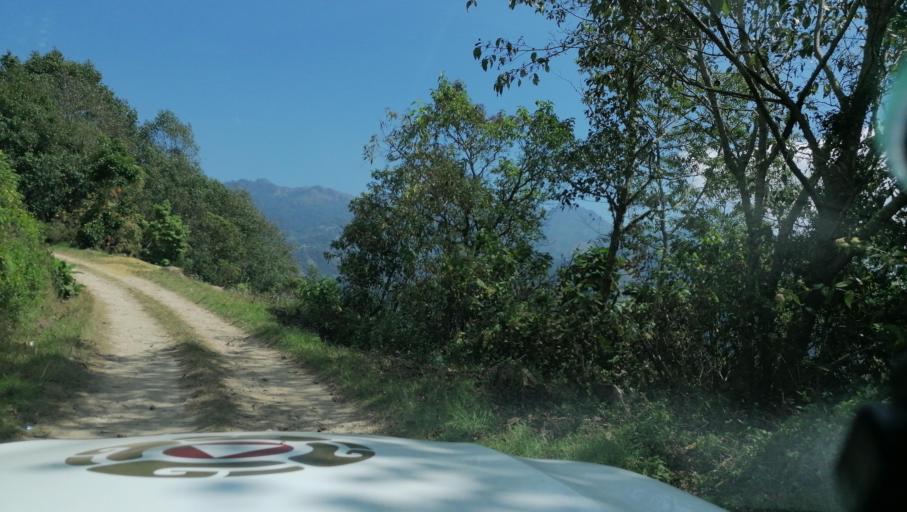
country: GT
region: San Marcos
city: Tacana
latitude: 15.2086
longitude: -92.2145
